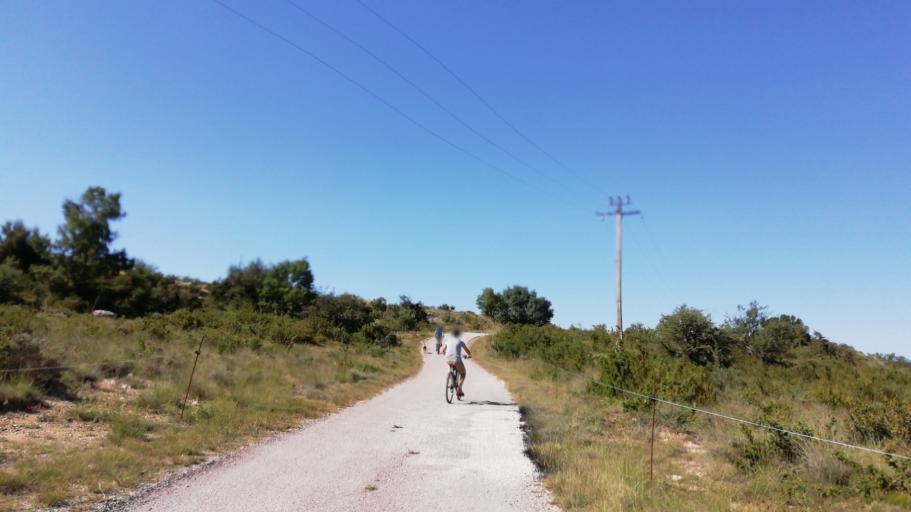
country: FR
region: Languedoc-Roussillon
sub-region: Departement de l'Herault
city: Saint-Martin-de-Londres
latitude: 43.7968
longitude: 3.7586
